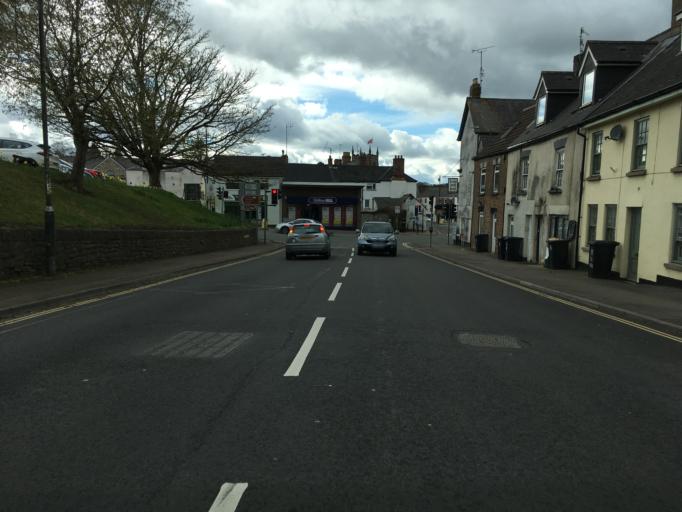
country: GB
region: England
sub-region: Gloucestershire
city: Coleford
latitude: 51.7941
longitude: -2.6156
